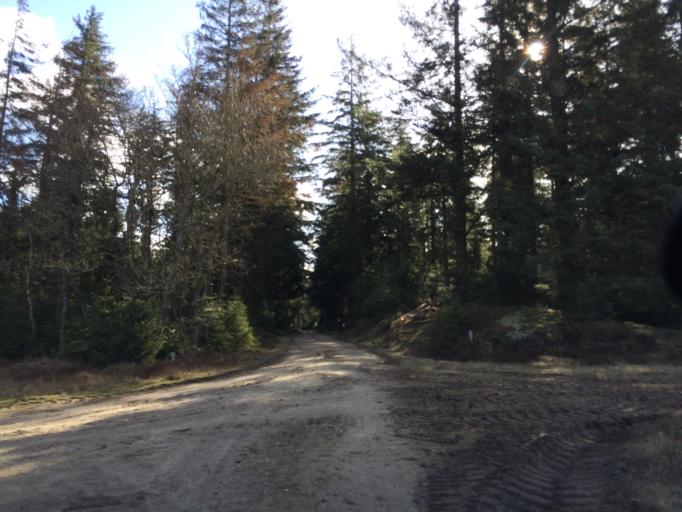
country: DK
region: Central Jutland
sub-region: Holstebro Kommune
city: Ulfborg
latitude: 56.2515
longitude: 8.4451
